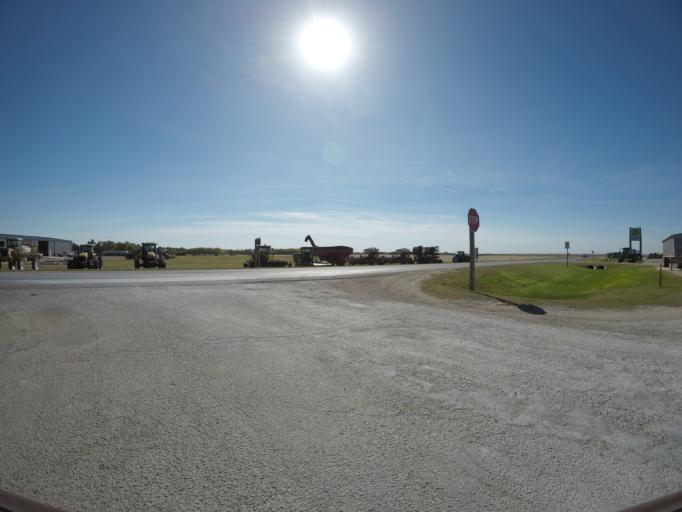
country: US
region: Kansas
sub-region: Smith County
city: Smith Center
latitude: 39.7845
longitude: -98.7966
